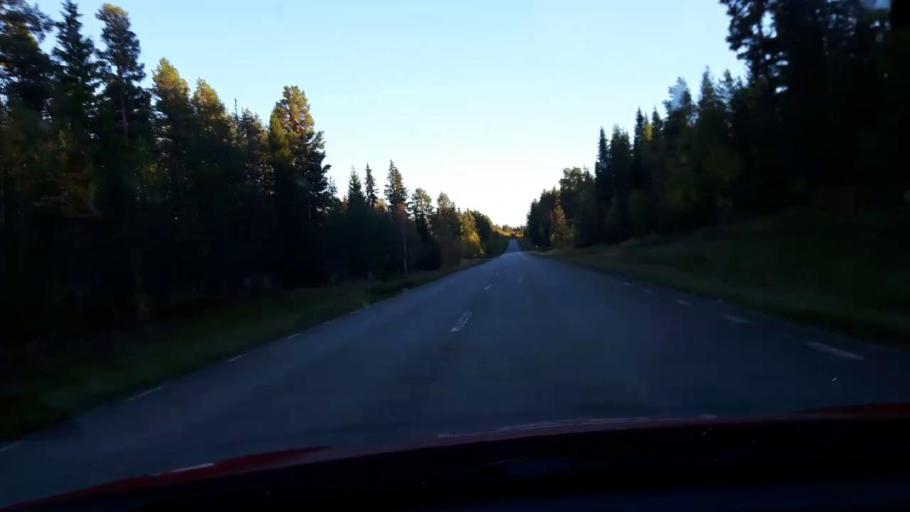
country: SE
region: Jaemtland
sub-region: Krokoms Kommun
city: Krokom
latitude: 63.4445
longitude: 14.4935
